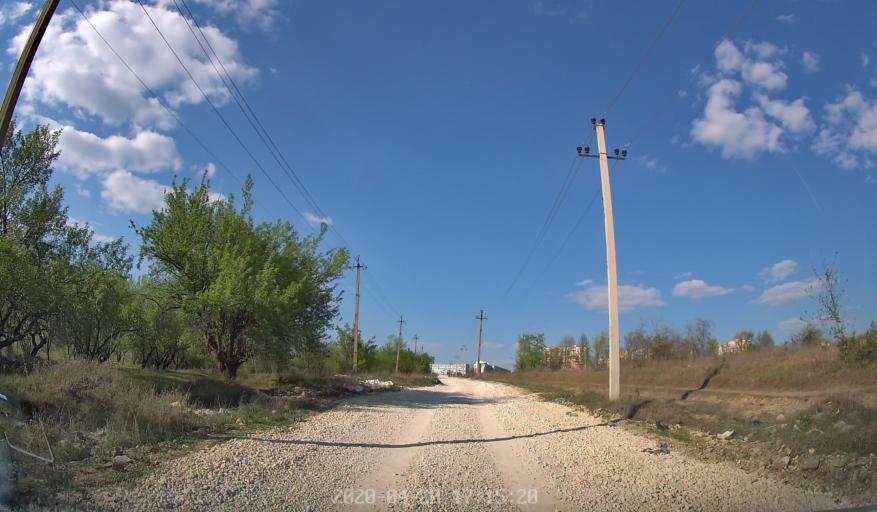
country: MD
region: Chisinau
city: Chisinau
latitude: 46.9695
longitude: 28.8445
